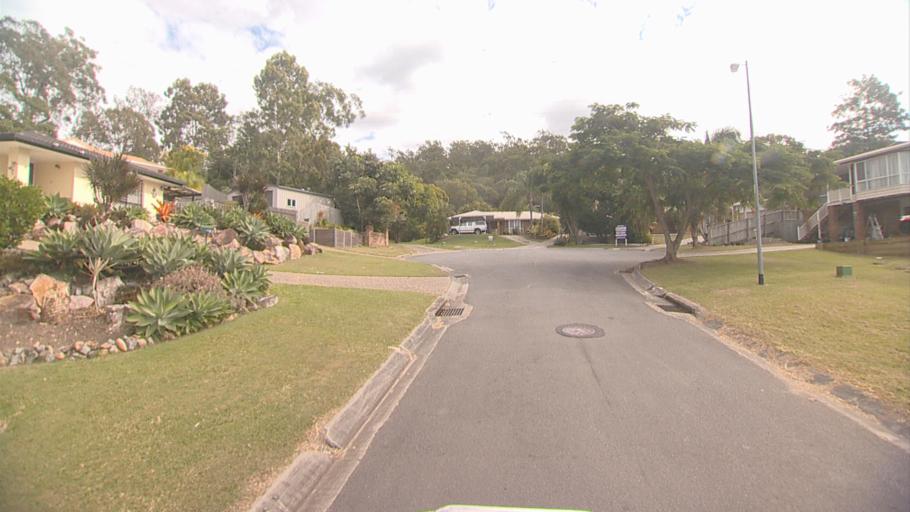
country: AU
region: Queensland
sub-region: Logan
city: Windaroo
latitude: -27.7319
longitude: 153.2035
